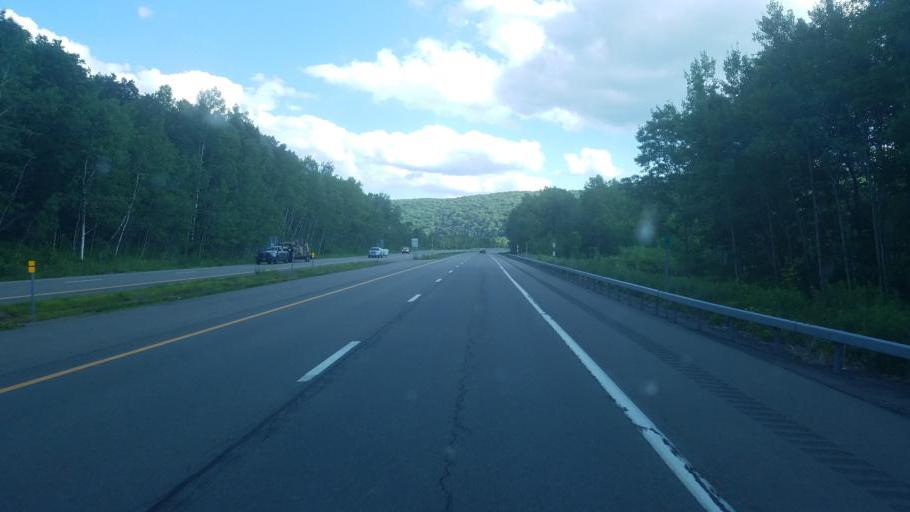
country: US
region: New York
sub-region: Cattaraugus County
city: Salamanca
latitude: 42.1172
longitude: -78.7781
